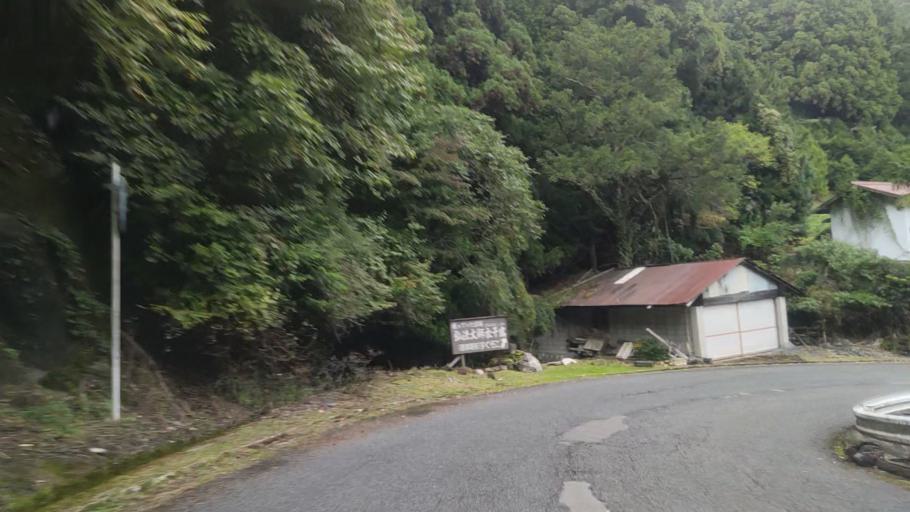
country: JP
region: Wakayama
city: Koya
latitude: 34.2271
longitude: 135.6194
